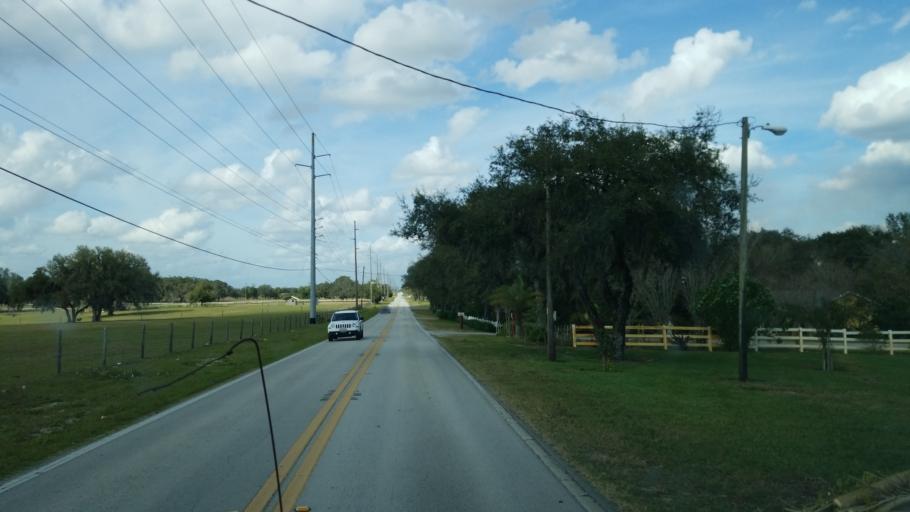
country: US
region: Florida
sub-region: Polk County
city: Haines City
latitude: 28.1270
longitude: -81.5904
